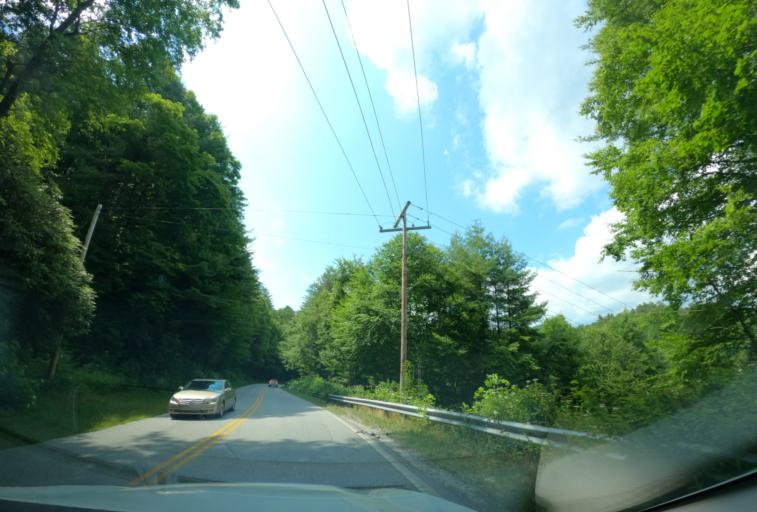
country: US
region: North Carolina
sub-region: Jackson County
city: Cullowhee
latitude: 35.0759
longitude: -82.9988
